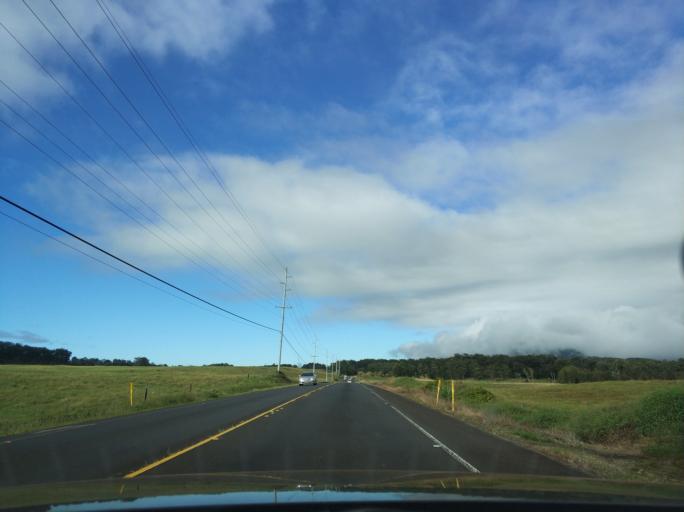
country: US
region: Hawaii
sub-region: Hawaii County
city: Waimea
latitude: 20.0472
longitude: -155.5809
